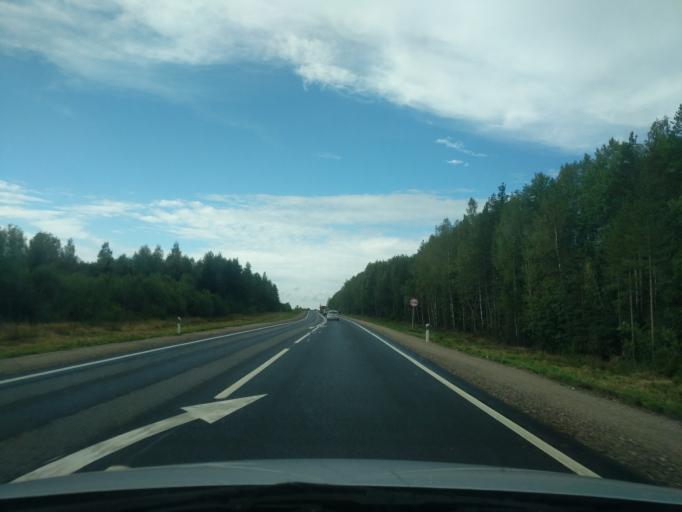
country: RU
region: Kostroma
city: Ostrovskoye
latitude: 57.8150
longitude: 41.9736
